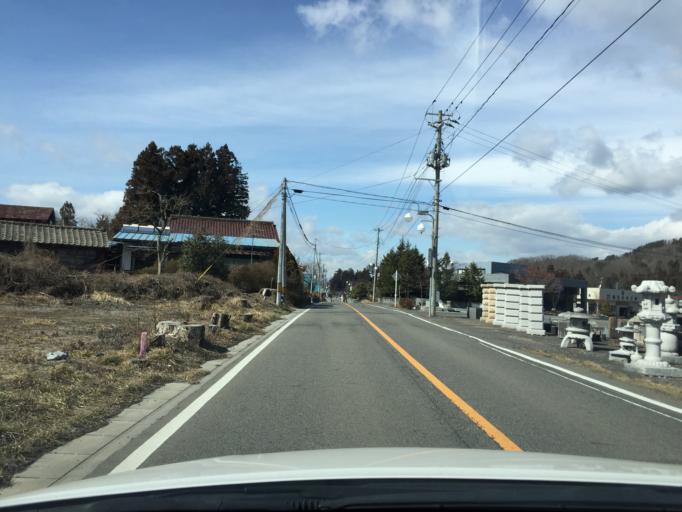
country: JP
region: Fukushima
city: Funehikimachi-funehiki
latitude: 37.3911
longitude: 140.5790
